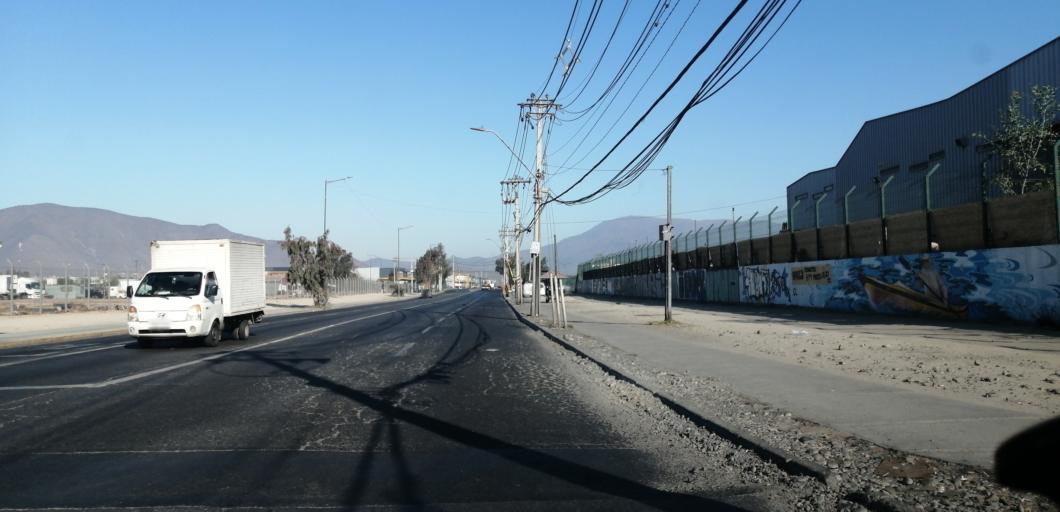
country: CL
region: Santiago Metropolitan
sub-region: Provincia de Santiago
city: Lo Prado
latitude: -33.4443
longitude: -70.7762
